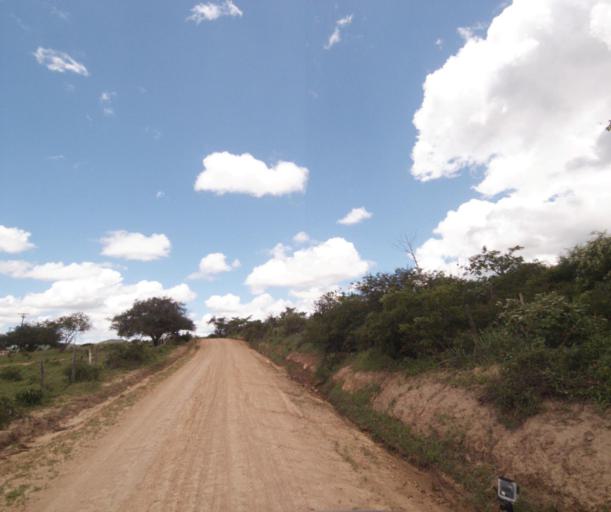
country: BR
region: Bahia
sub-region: Pocoes
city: Pocoes
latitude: -14.3794
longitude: -40.3639
